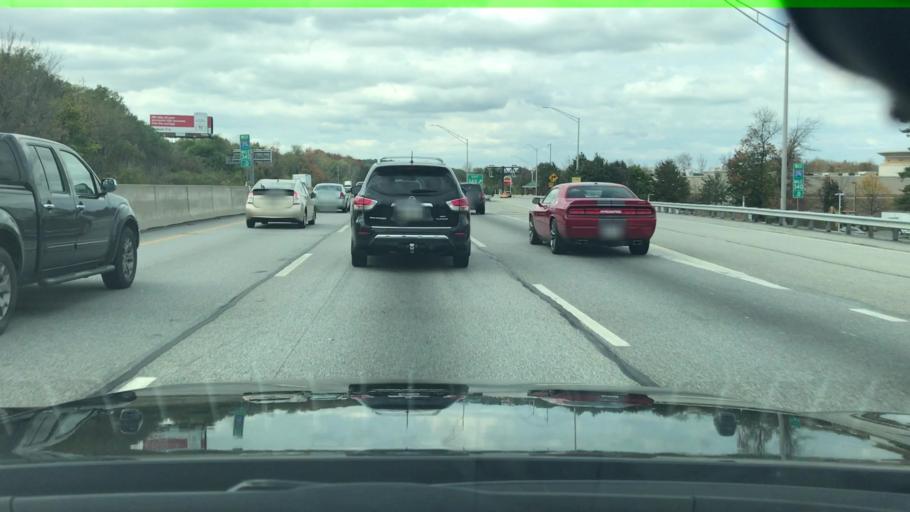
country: US
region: Pennsylvania
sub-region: Montgomery County
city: Dresher
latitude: 40.1400
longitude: -75.1670
